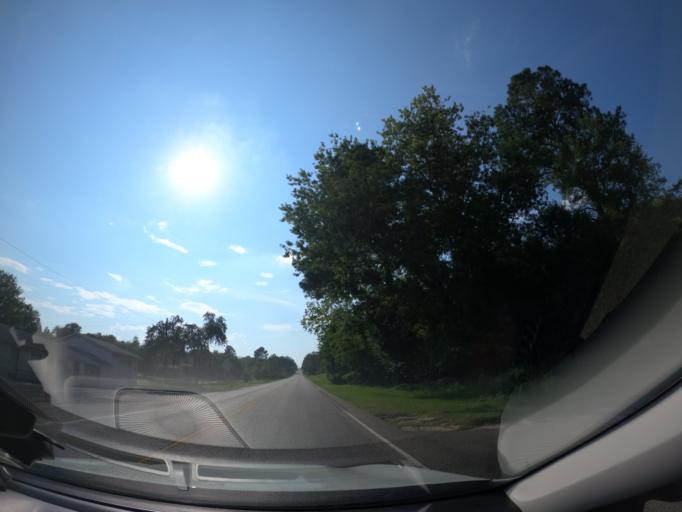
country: US
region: South Carolina
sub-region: Aiken County
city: Jackson
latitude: 33.4080
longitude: -81.7891
